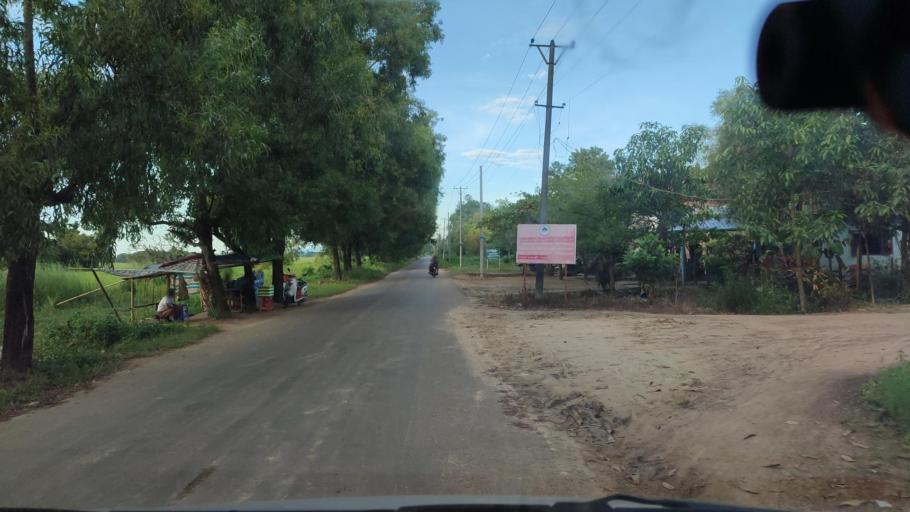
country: MM
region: Bago
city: Tharyarwady
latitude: 17.6982
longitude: 95.7823
